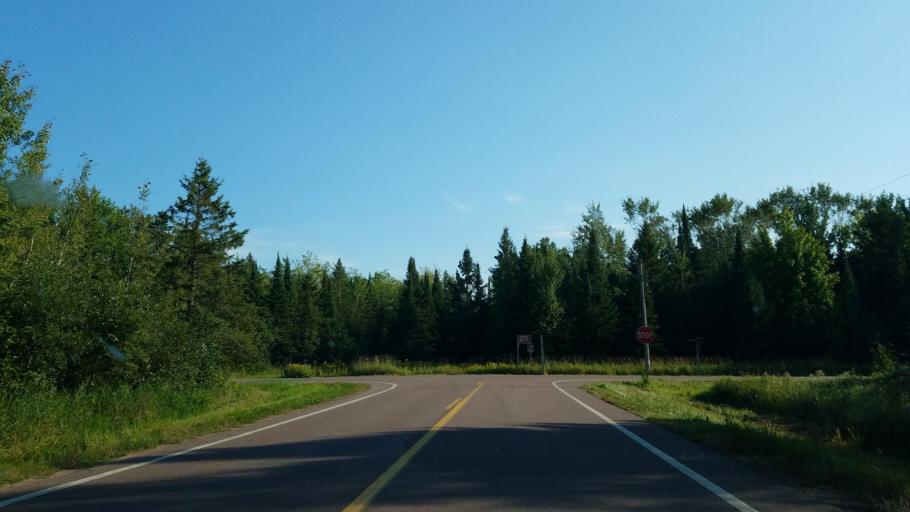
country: US
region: Wisconsin
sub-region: Bayfield County
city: Washburn
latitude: 46.7888
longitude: -90.7162
